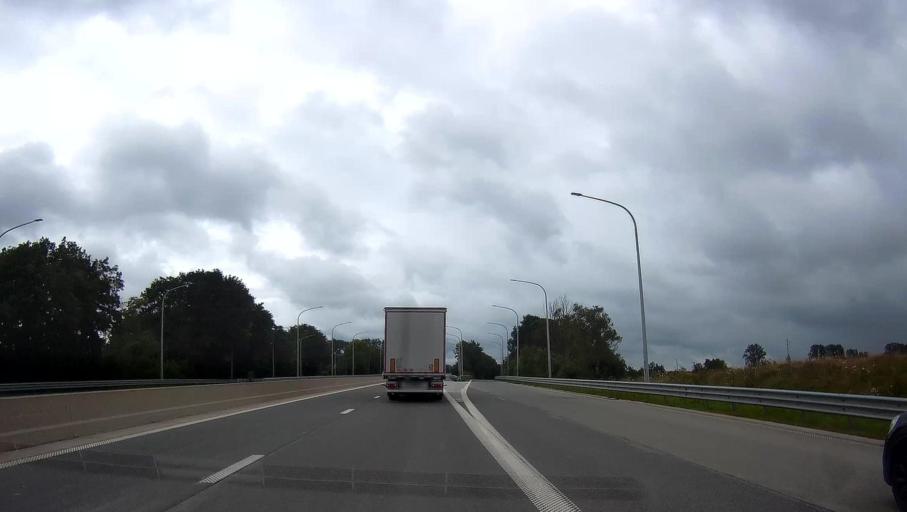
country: BE
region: Wallonia
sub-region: Province de Namur
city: Philippeville
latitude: 50.1993
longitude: 4.5282
